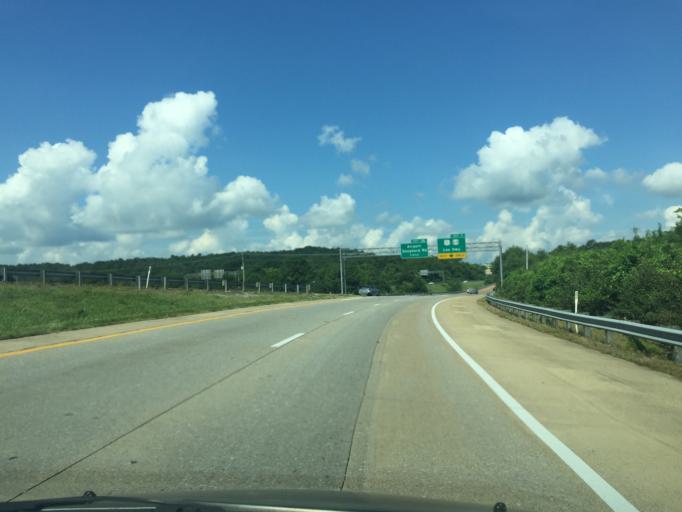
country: US
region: Tennessee
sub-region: Hamilton County
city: East Brainerd
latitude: 35.0284
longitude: -85.1742
